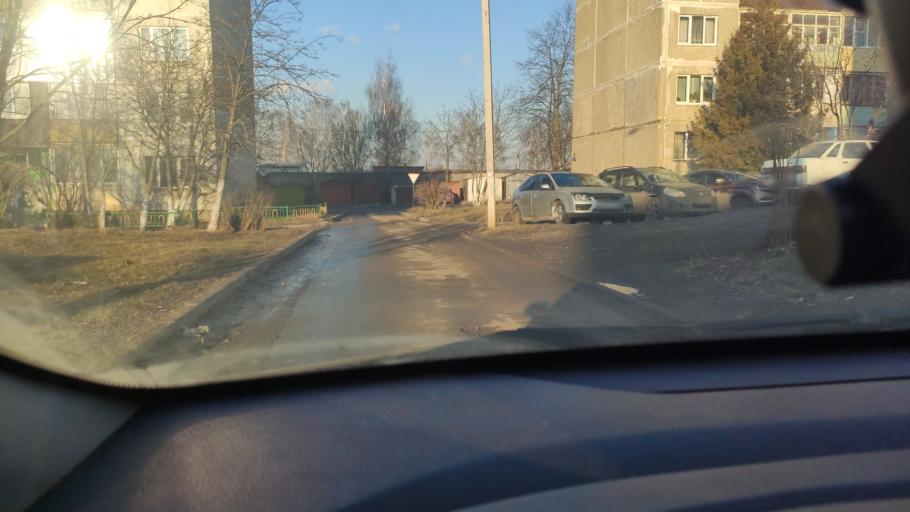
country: RU
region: Moskovskaya
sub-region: Chekhovskiy Rayon
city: Chekhov
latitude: 55.1666
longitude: 37.4368
